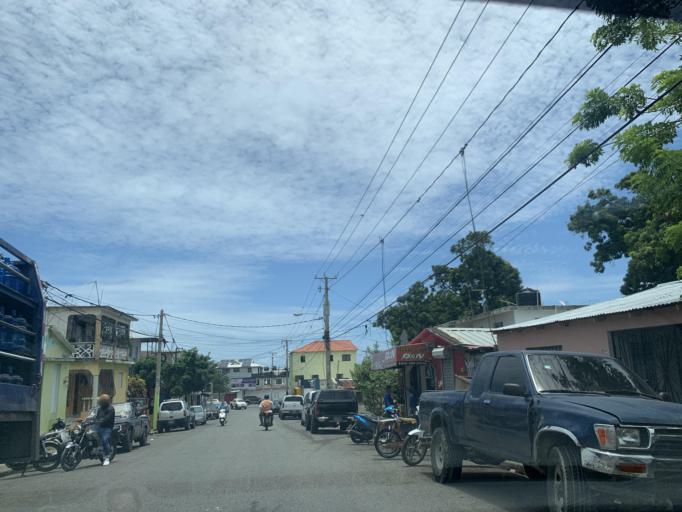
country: DO
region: Puerto Plata
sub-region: Puerto Plata
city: Puerto Plata
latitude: 19.7881
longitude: -70.6866
